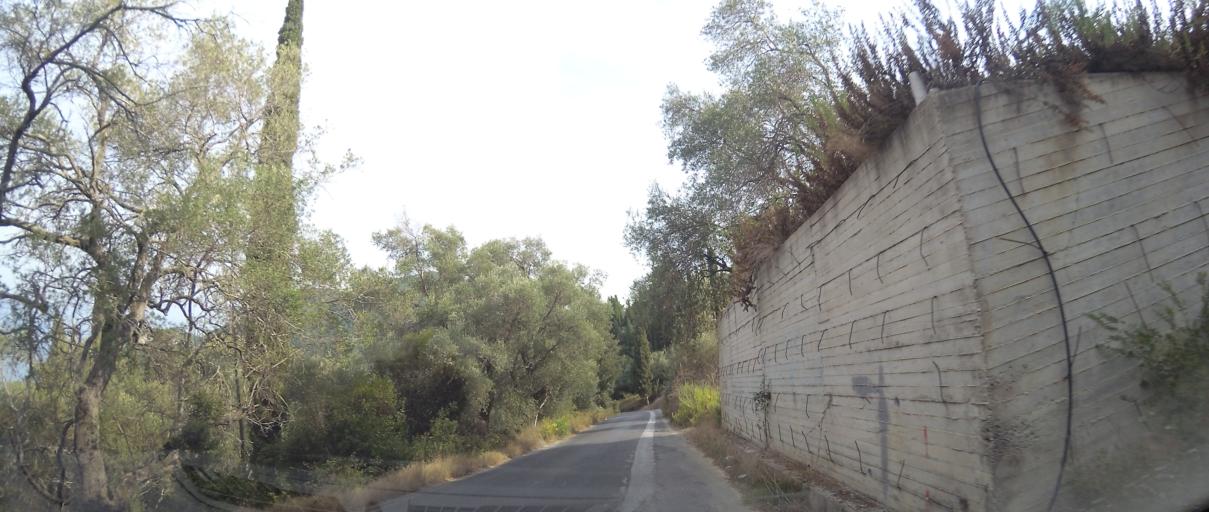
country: GR
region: Ionian Islands
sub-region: Nomos Kerkyras
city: Kynopiastes
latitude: 39.5569
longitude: 19.8592
